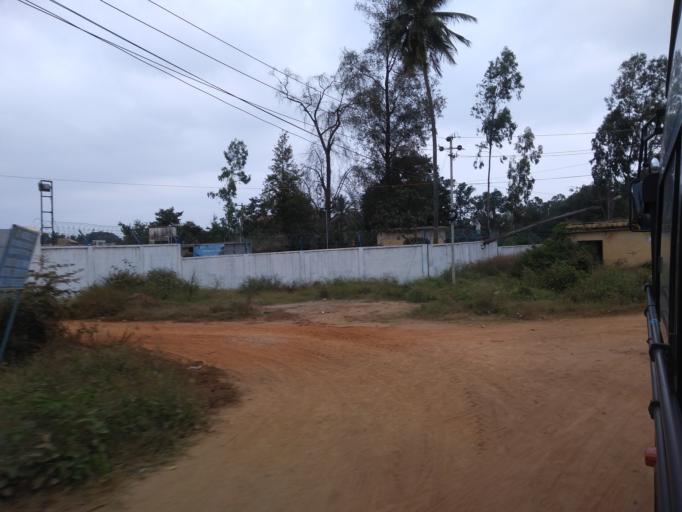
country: IN
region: Karnataka
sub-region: Bangalore Rural
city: Nelamangala
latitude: 13.1009
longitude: 77.4836
